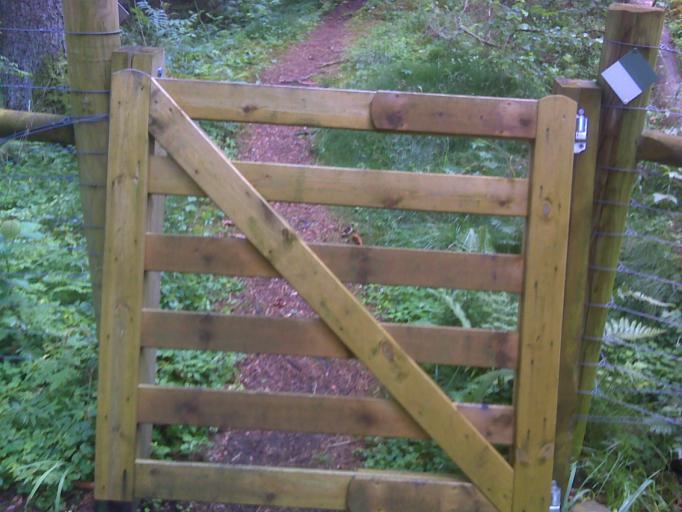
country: SE
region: Vaestra Goetaland
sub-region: Lysekils Kommun
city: Brastad
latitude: 58.4437
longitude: 11.4299
